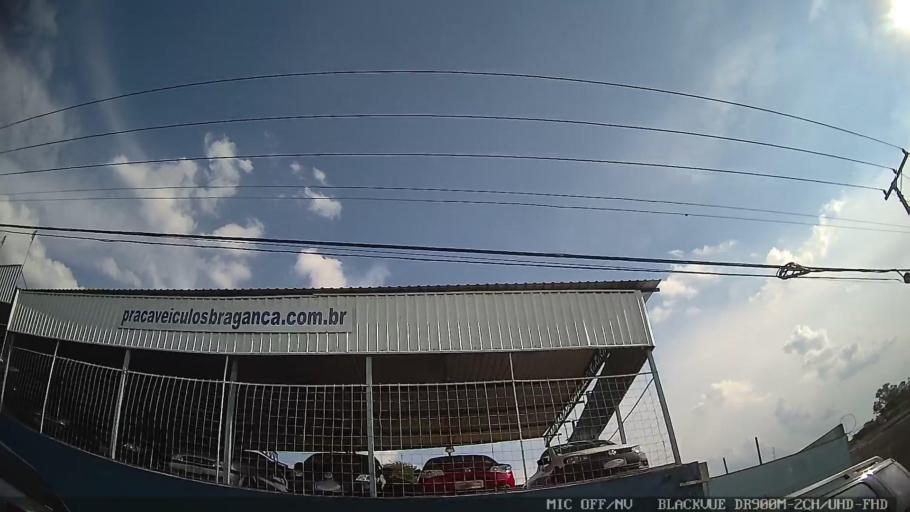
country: BR
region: Sao Paulo
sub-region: Braganca Paulista
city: Braganca Paulista
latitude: -22.9334
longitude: -46.5342
